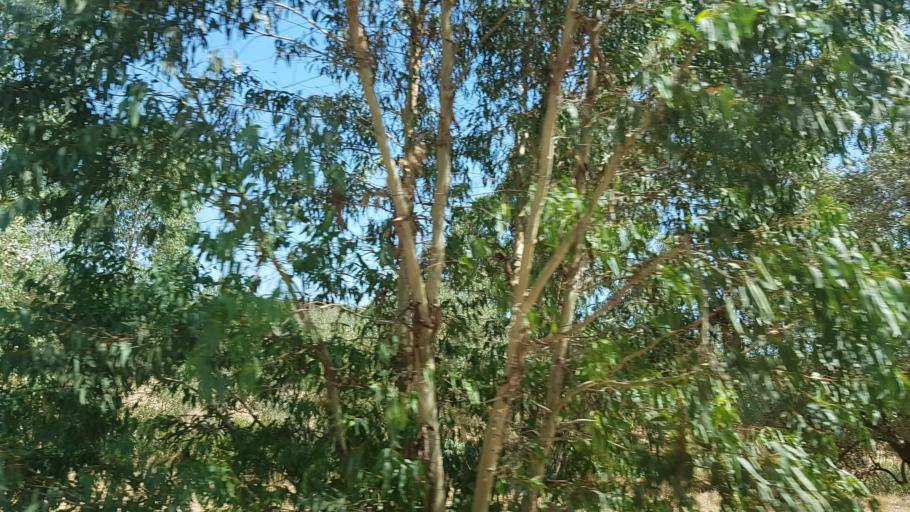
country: TR
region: Mugla
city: Karaova
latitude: 37.0761
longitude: 27.6748
